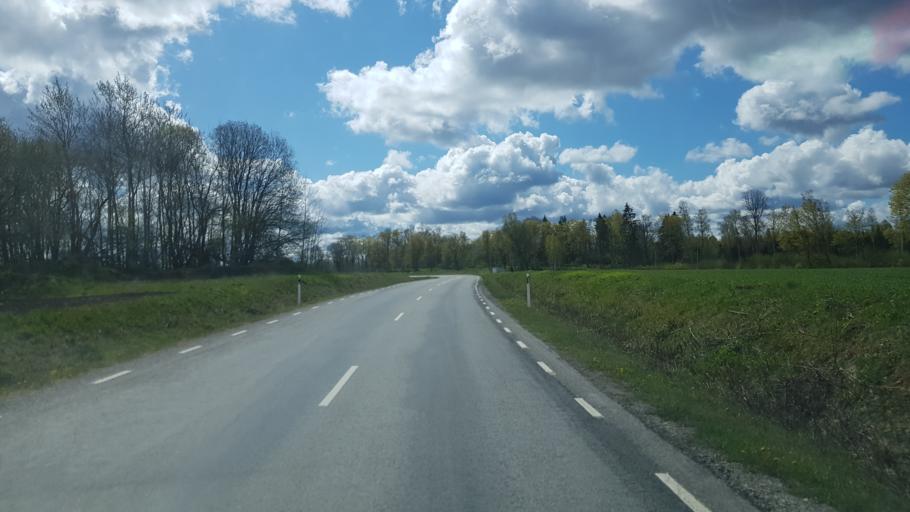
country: EE
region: Harju
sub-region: Raasiku vald
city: Raasiku
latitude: 59.0921
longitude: 25.1730
